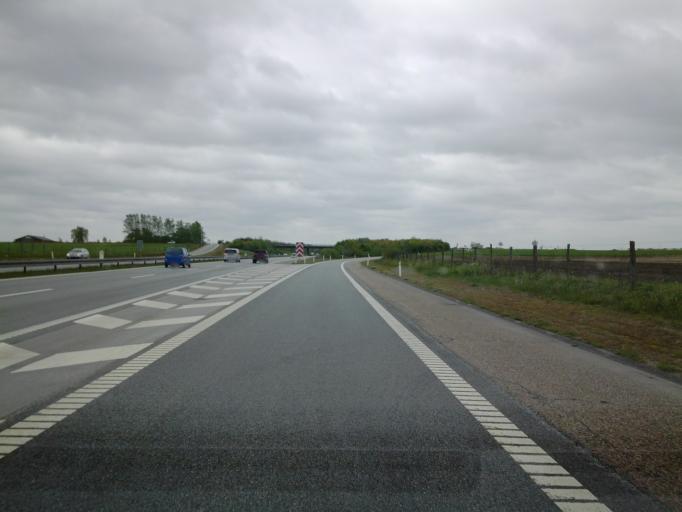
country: DK
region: North Denmark
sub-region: Bronderslev Kommune
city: Hjallerup
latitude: 57.1723
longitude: 10.1926
